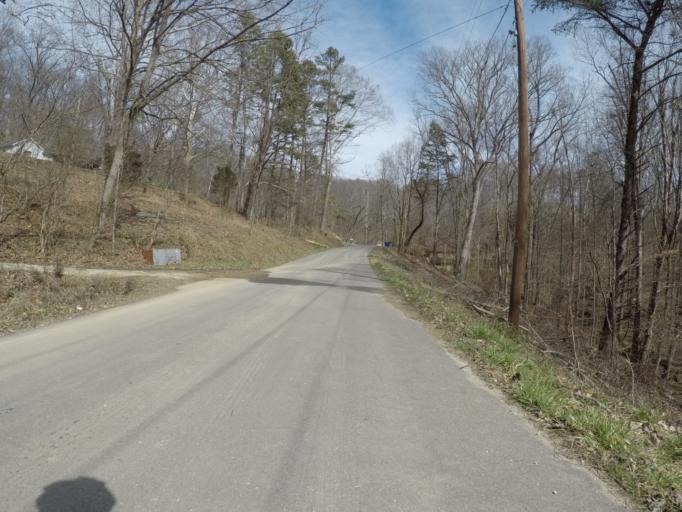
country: US
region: West Virginia
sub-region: Wayne County
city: Ceredo
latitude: 38.3738
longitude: -82.5433
